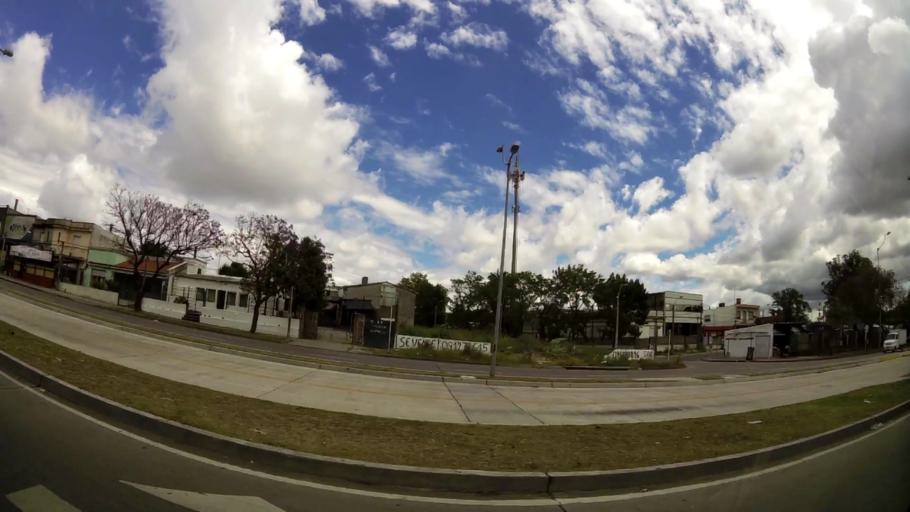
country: UY
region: Montevideo
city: Montevideo
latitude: -34.8516
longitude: -56.1595
